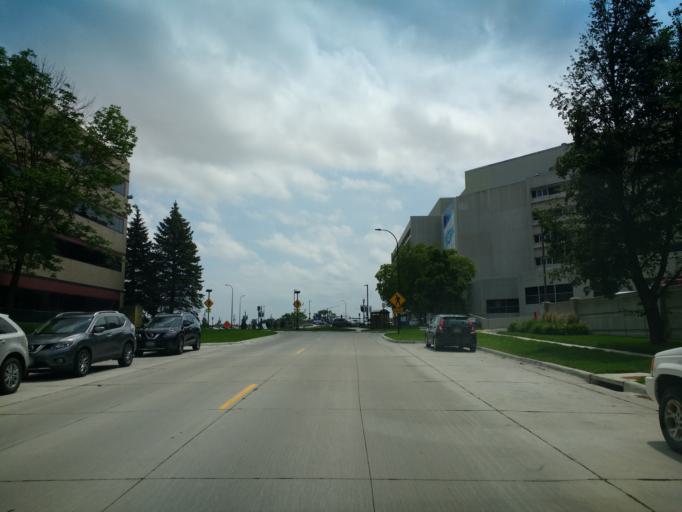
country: US
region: Iowa
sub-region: Woodbury County
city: Sioux City
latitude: 42.5203
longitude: -96.4052
